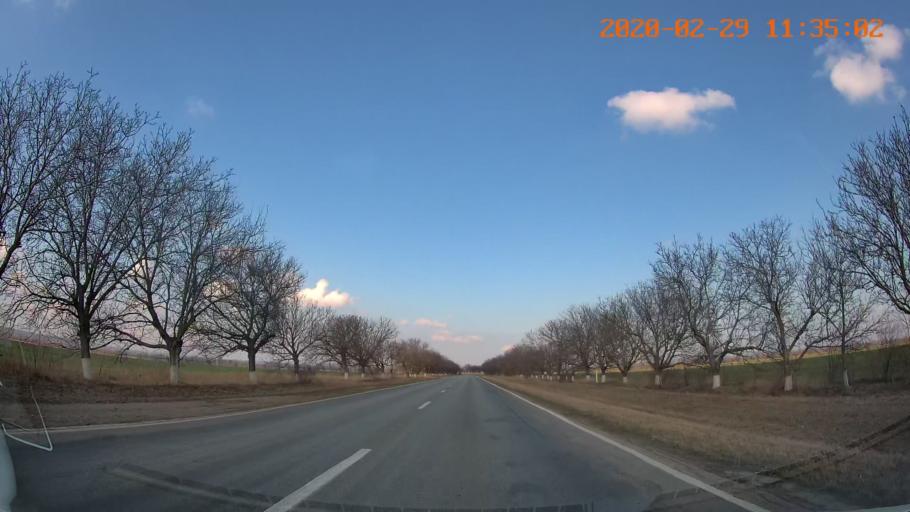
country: MD
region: Rezina
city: Saharna
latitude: 47.5744
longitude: 29.0673
